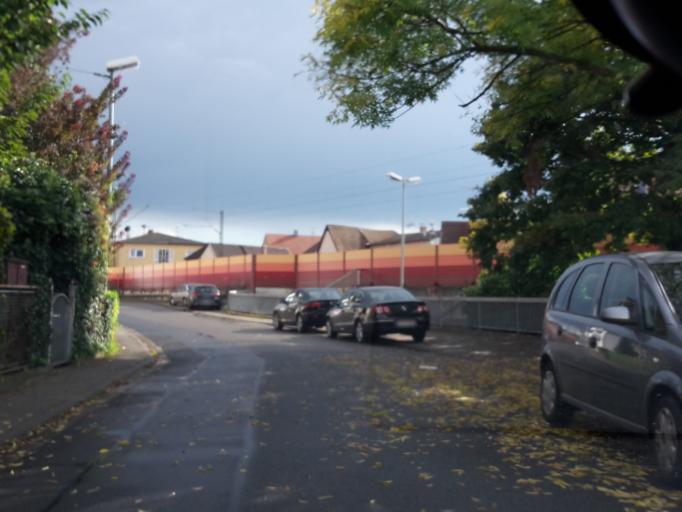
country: DE
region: Rheinland-Pfalz
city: Nackenheim
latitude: 49.9174
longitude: 8.3455
